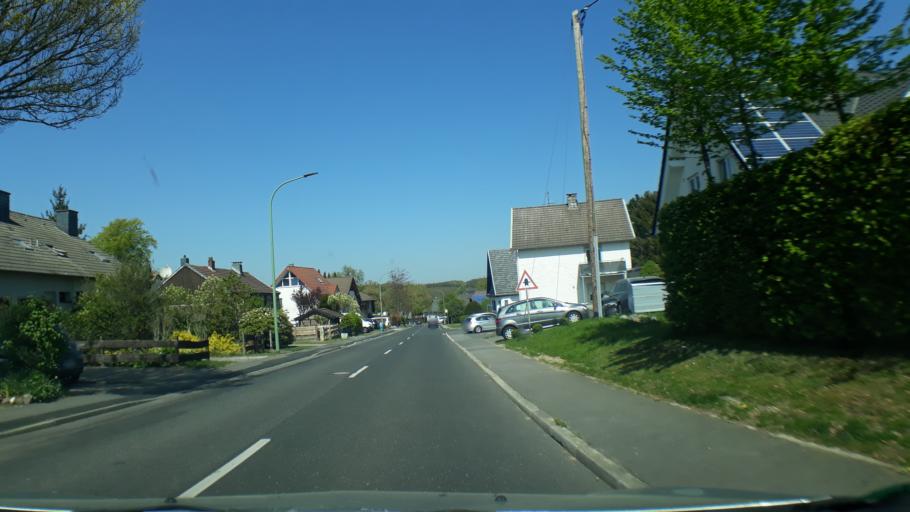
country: DE
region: North Rhine-Westphalia
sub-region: Regierungsbezirk Koln
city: Roetgen
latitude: 50.6488
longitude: 6.2000
